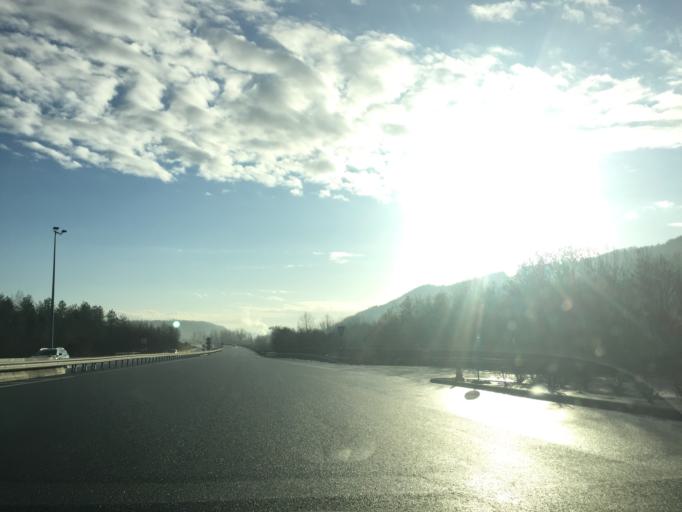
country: FR
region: Aquitaine
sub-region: Departement de la Dordogne
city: Montignac
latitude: 45.1501
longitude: 1.1700
